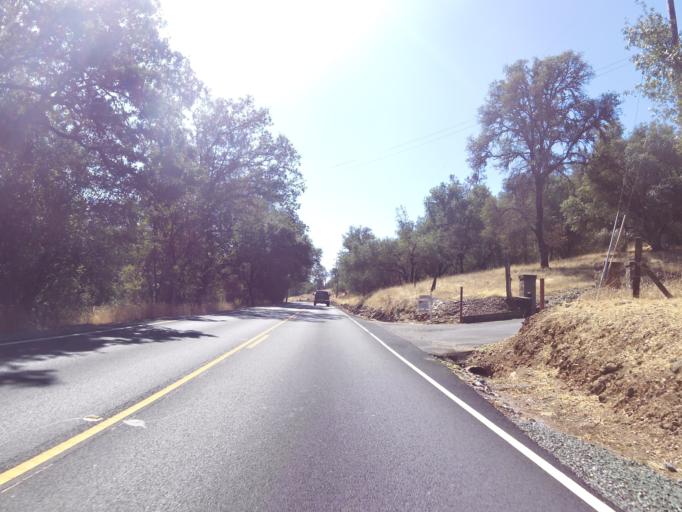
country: US
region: California
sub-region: El Dorado County
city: Deer Park
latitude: 38.5838
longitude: -120.8460
